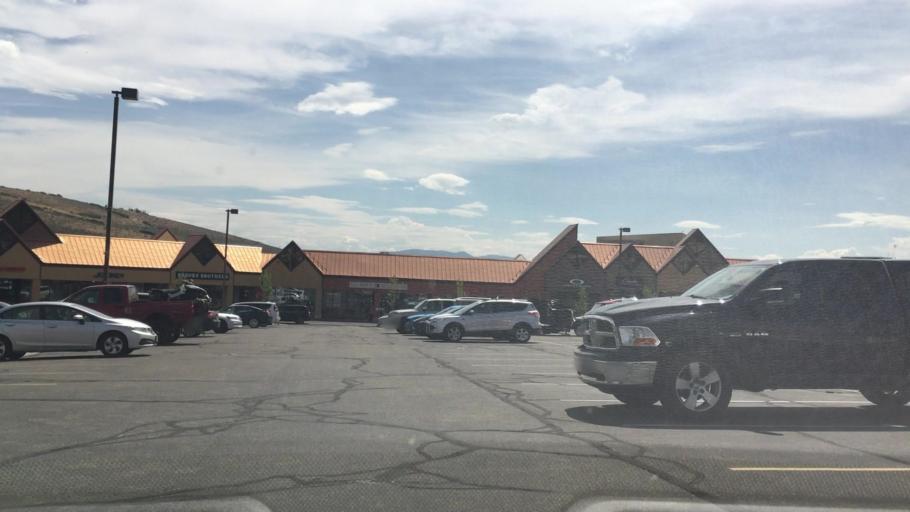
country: US
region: Utah
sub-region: Summit County
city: Snyderville
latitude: 40.7293
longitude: -111.5514
